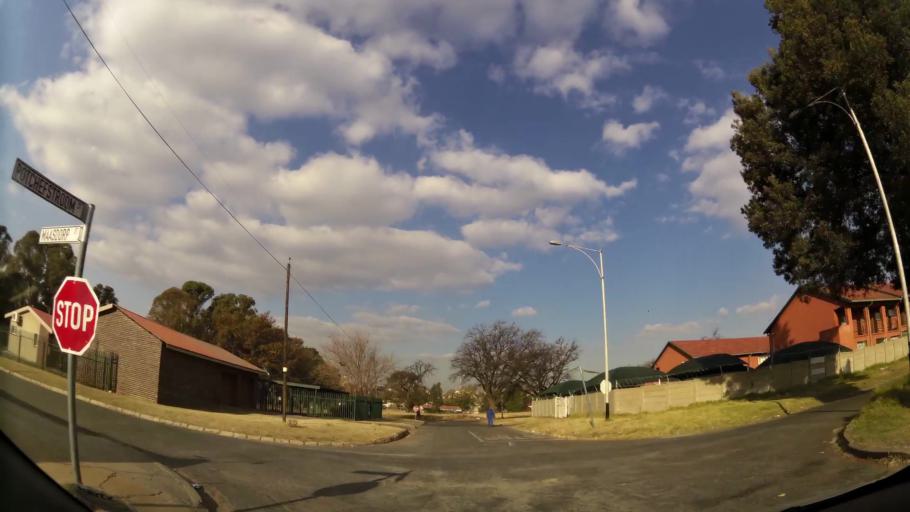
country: ZA
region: Gauteng
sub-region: West Rand District Municipality
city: Krugersdorp
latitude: -26.0992
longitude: 27.7615
